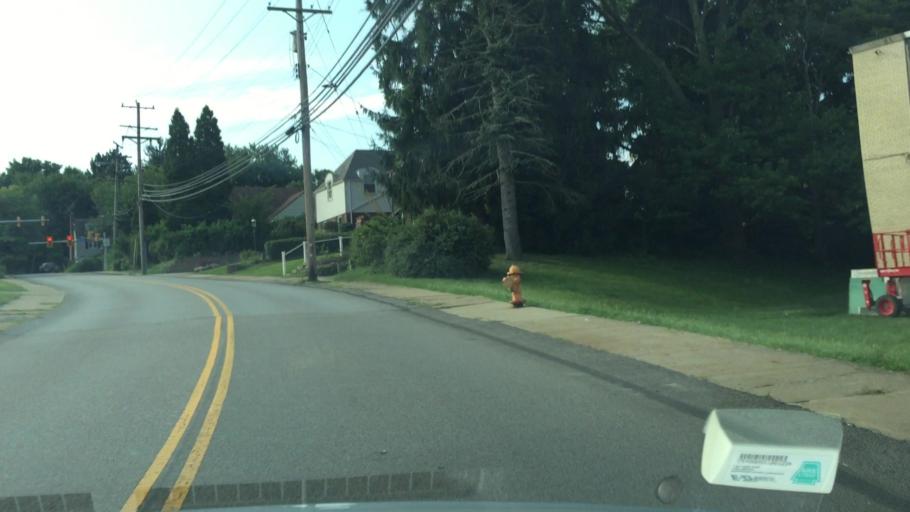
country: US
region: Pennsylvania
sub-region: Allegheny County
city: Heidelberg
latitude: 40.3725
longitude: -80.0836
